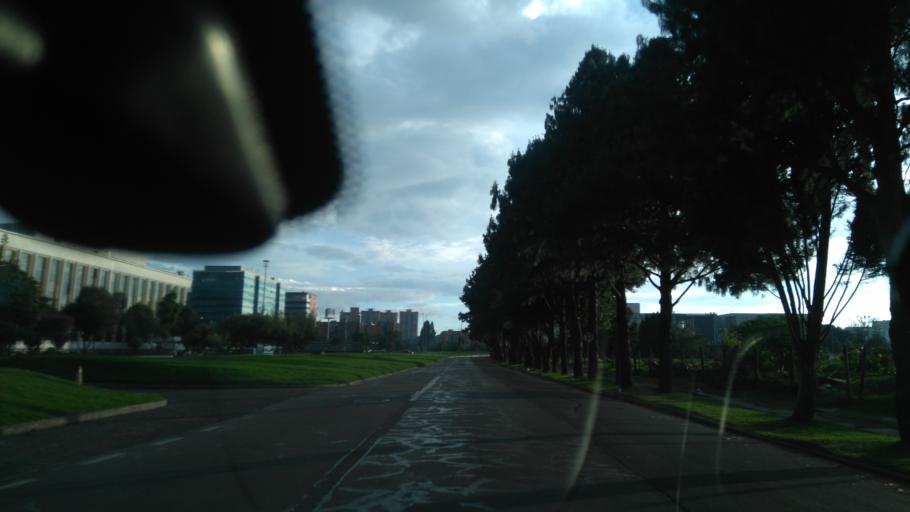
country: CO
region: Bogota D.C.
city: Bogota
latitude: 4.6491
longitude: -74.0974
